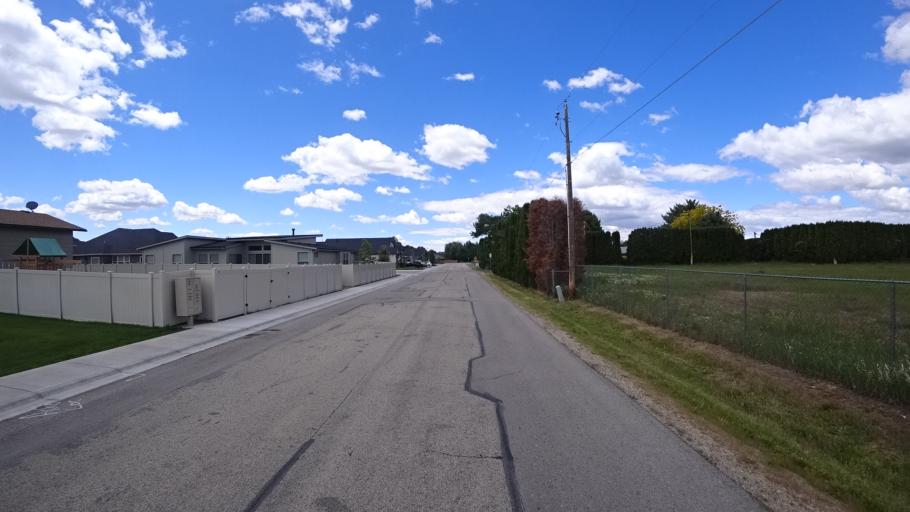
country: US
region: Idaho
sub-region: Ada County
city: Eagle
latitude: 43.6448
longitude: -116.3420
